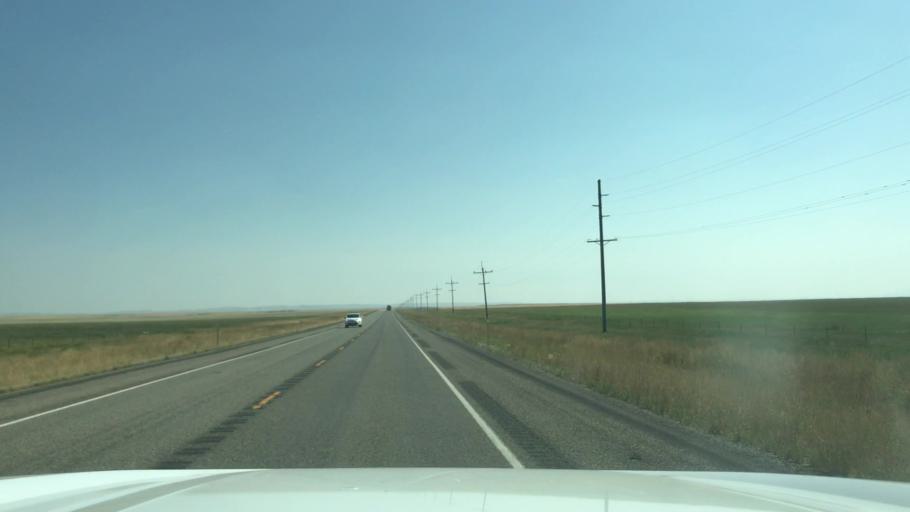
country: US
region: Montana
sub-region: Wheatland County
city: Harlowton
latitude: 46.5159
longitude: -109.7660
